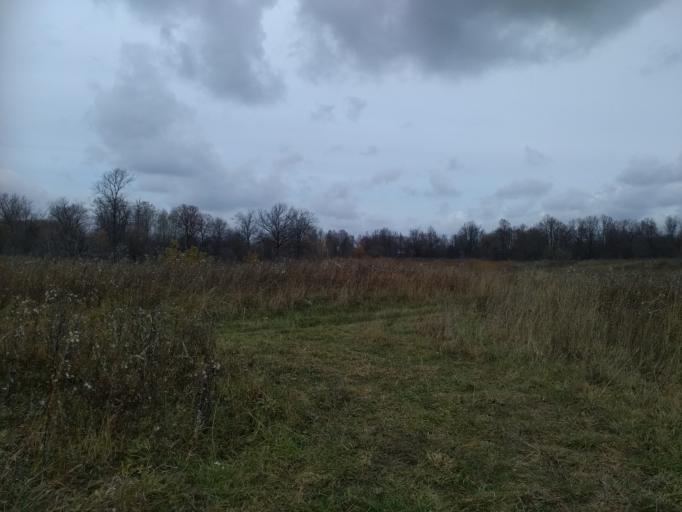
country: RU
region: Bashkortostan
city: Iglino
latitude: 54.7566
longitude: 56.5056
